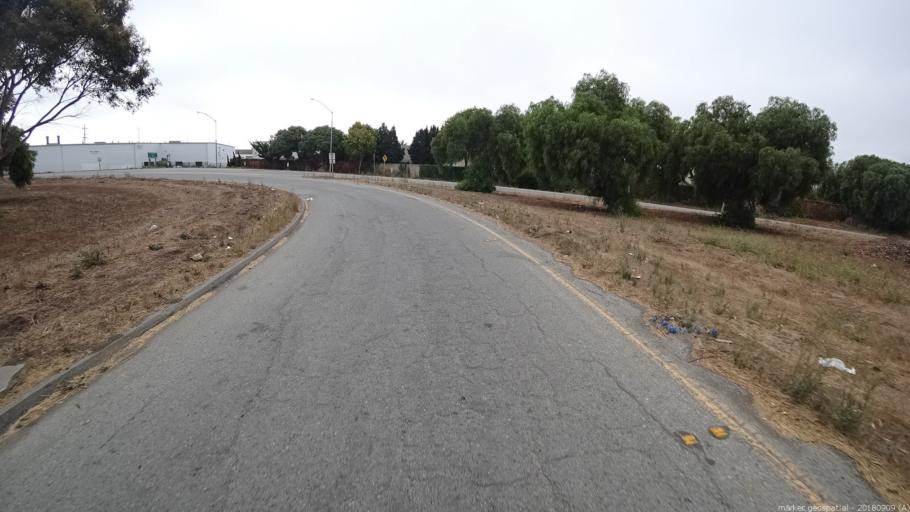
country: US
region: California
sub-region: Monterey County
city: Boronda
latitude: 36.6833
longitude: -121.6746
